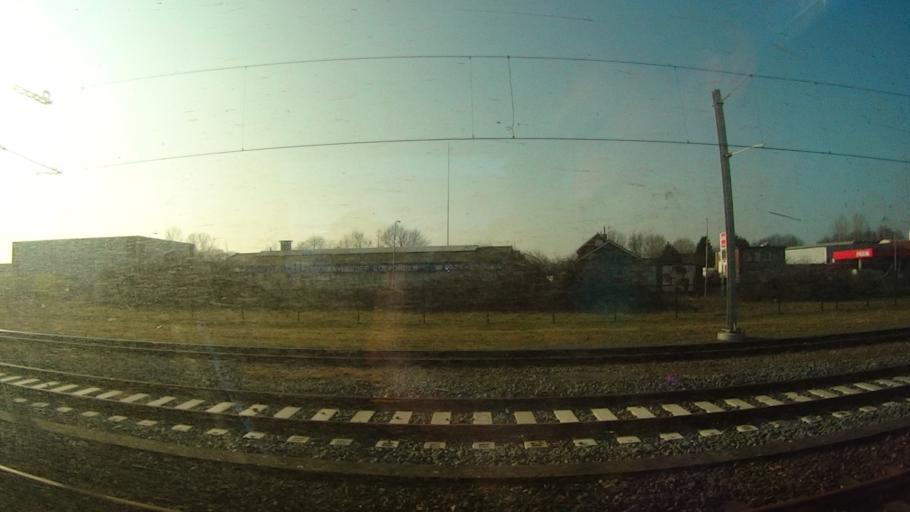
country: NL
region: Drenthe
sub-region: Gemeente Coevorden
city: Coevorden
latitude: 52.6642
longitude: 6.7353
